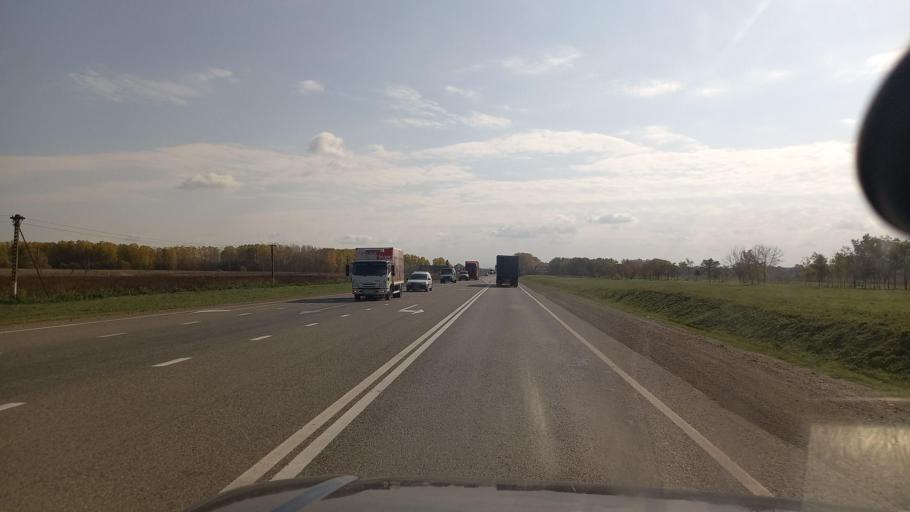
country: RU
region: Krasnodarskiy
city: Novoukrainskiy
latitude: 44.8890
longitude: 38.0763
